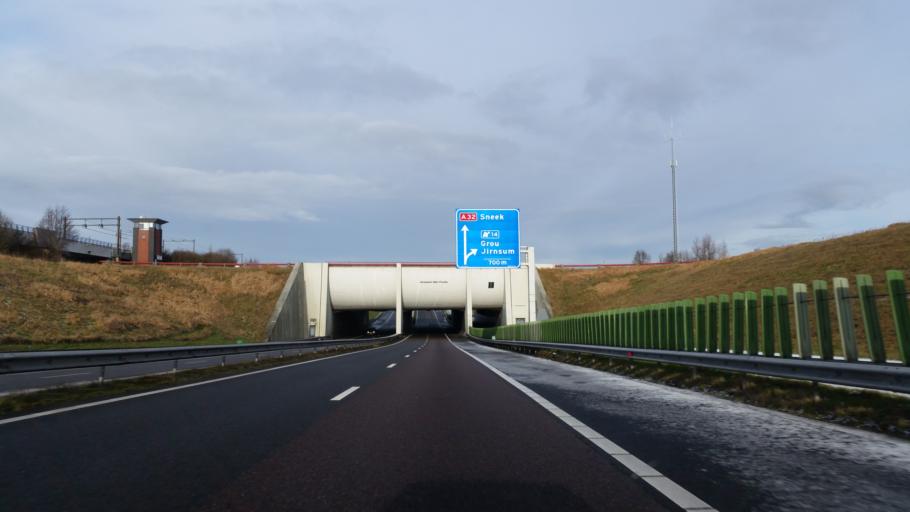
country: NL
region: Friesland
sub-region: Gemeente Boarnsterhim
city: Grou
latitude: 53.0776
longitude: 5.8300
